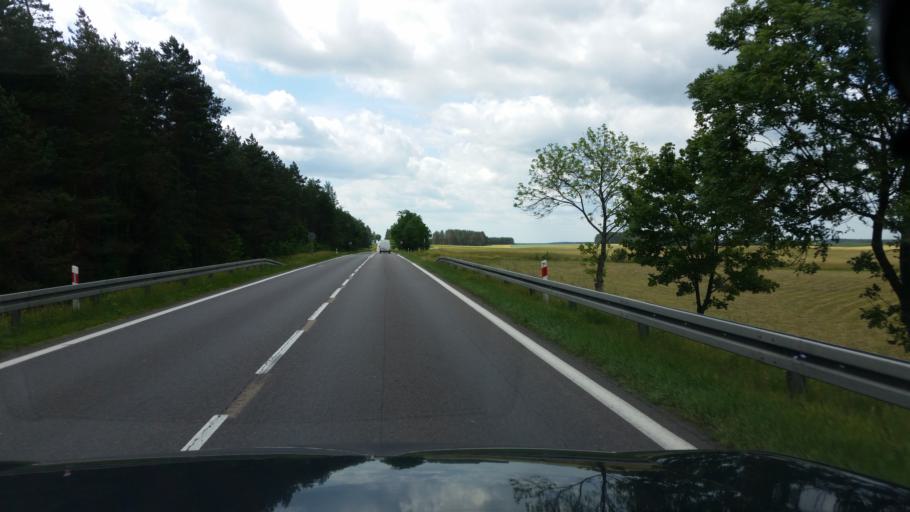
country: PL
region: Podlasie
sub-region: Powiat kolnenski
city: Stawiski
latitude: 53.4432
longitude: 22.1801
